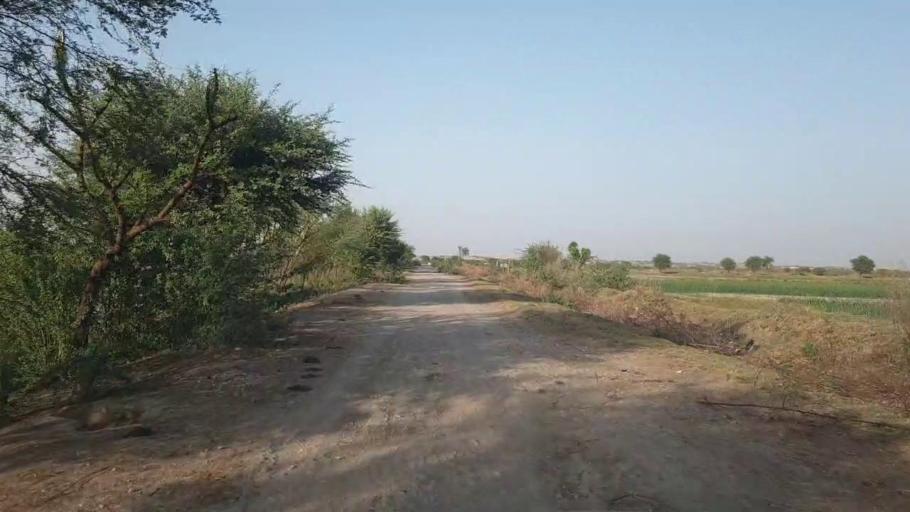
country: PK
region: Sindh
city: Dhoro Naro
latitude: 25.4963
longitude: 69.5835
